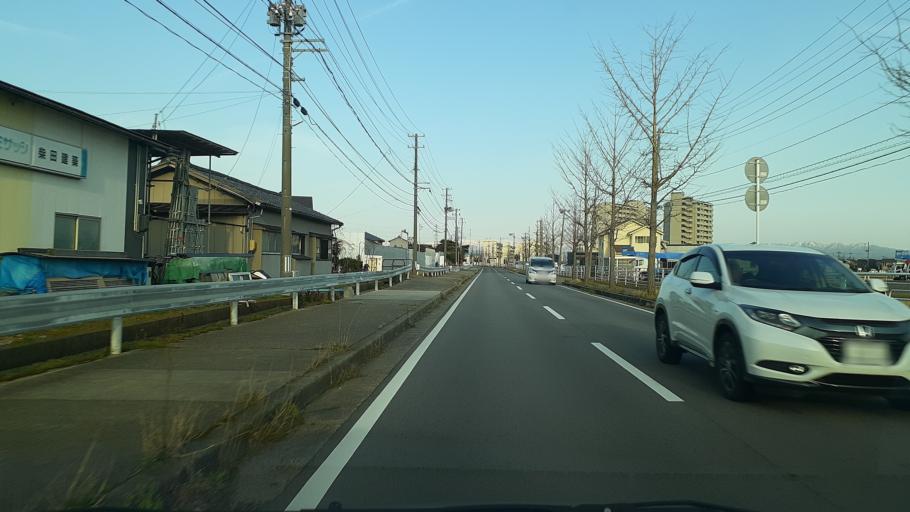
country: JP
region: Niigata
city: Niigata-shi
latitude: 37.8679
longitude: 139.0343
